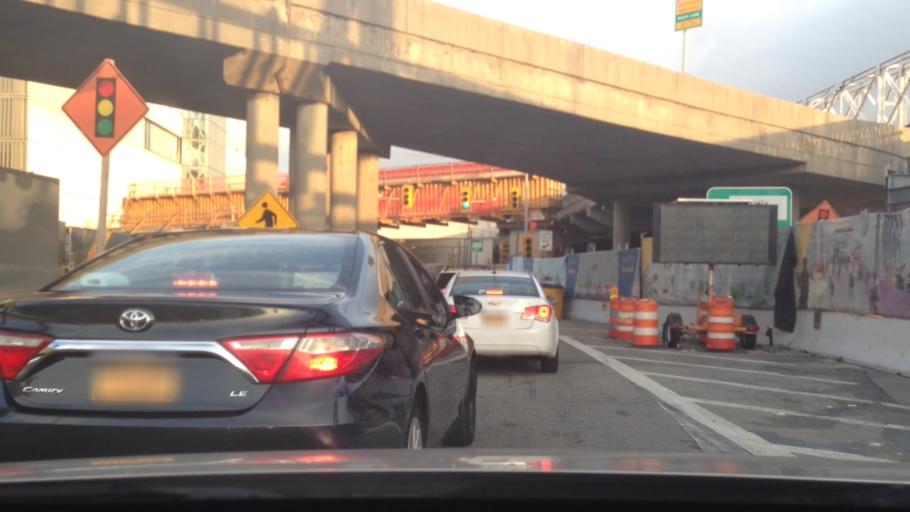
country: US
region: New York
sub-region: Bronx
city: The Bronx
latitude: 40.7694
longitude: -73.8638
